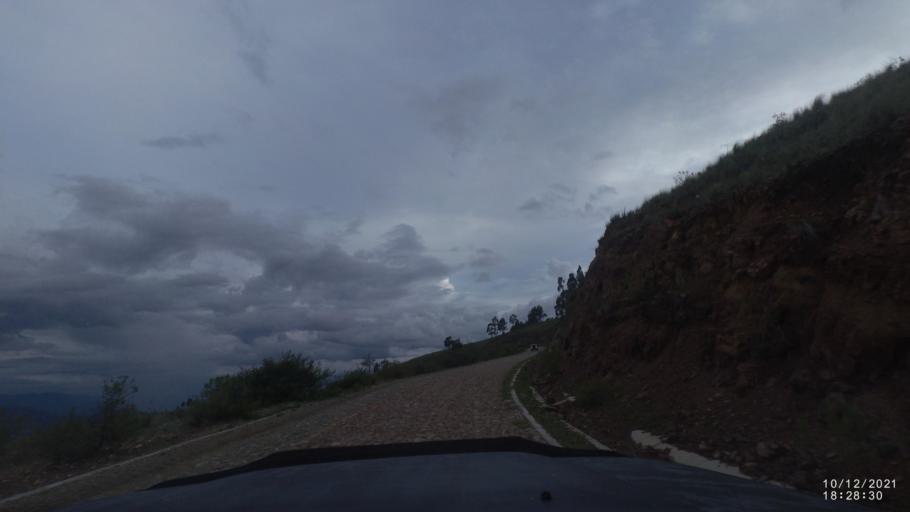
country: BO
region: Cochabamba
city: Tarata
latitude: -17.8082
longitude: -65.9757
